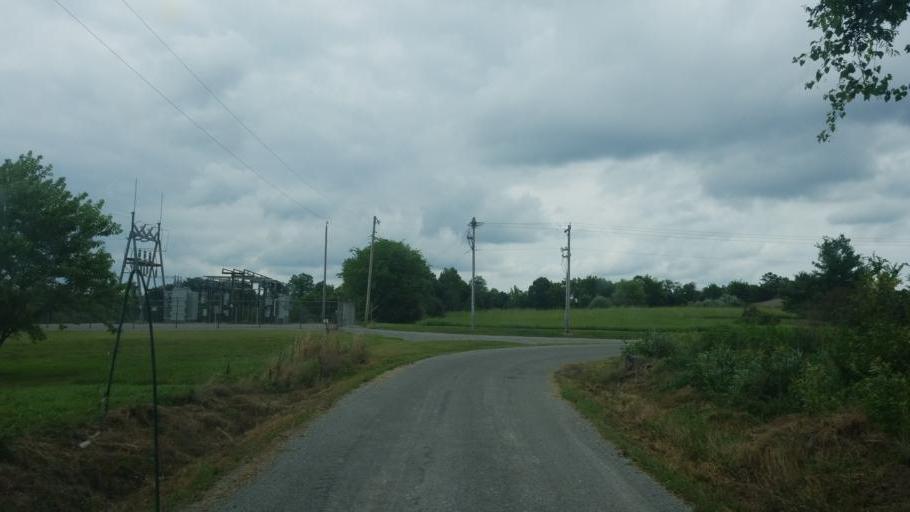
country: US
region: Illinois
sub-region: Jackson County
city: Murphysboro
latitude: 37.7131
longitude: -89.3277
